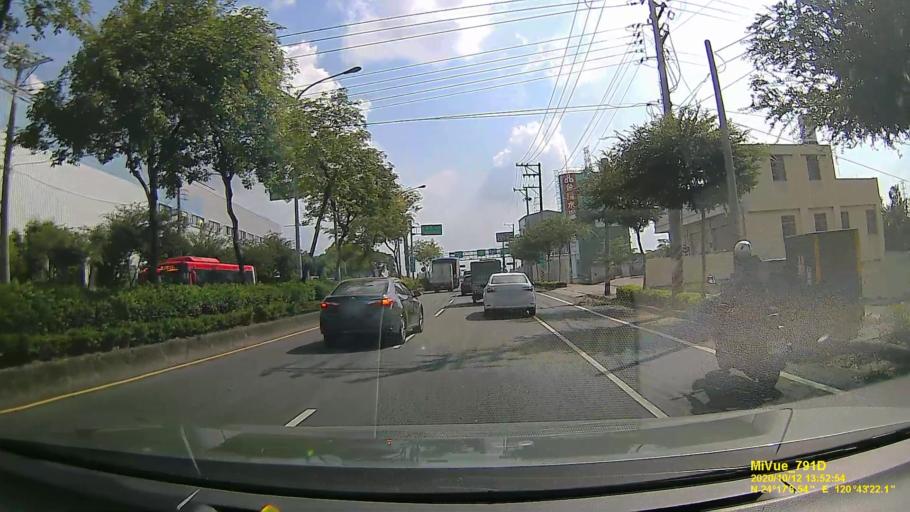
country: TW
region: Taiwan
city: Fengyuan
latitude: 24.2856
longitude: 120.7228
